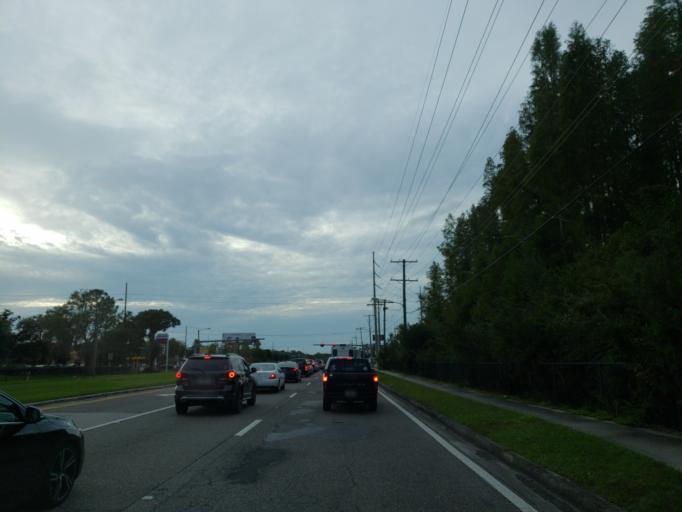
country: US
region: Florida
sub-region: Hillsborough County
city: Citrus Park
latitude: 28.0633
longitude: -82.5483
